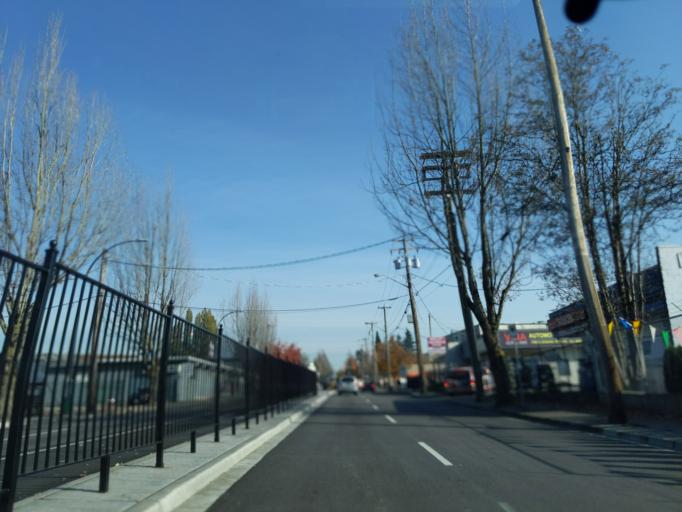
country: CA
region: British Columbia
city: New Westminster
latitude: 49.1988
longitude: -122.8486
